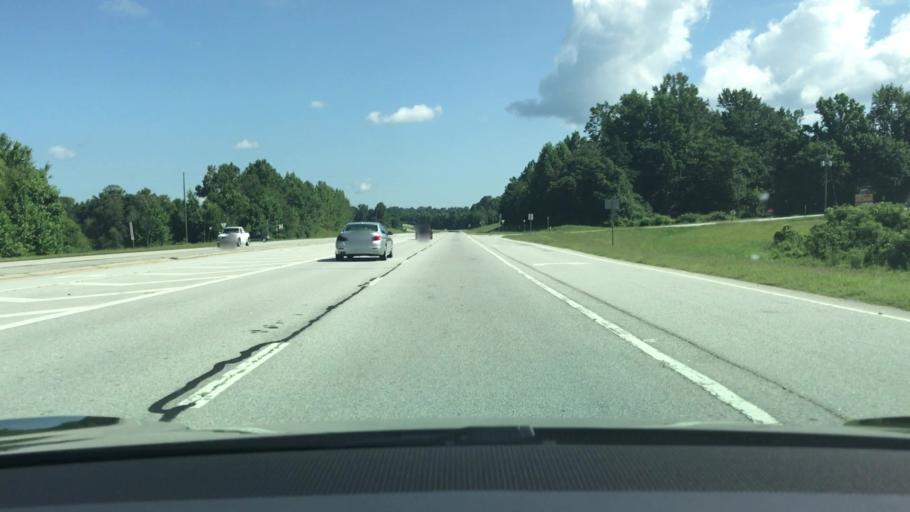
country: US
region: Georgia
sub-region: Habersham County
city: Clarkesville
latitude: 34.6132
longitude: -83.4488
